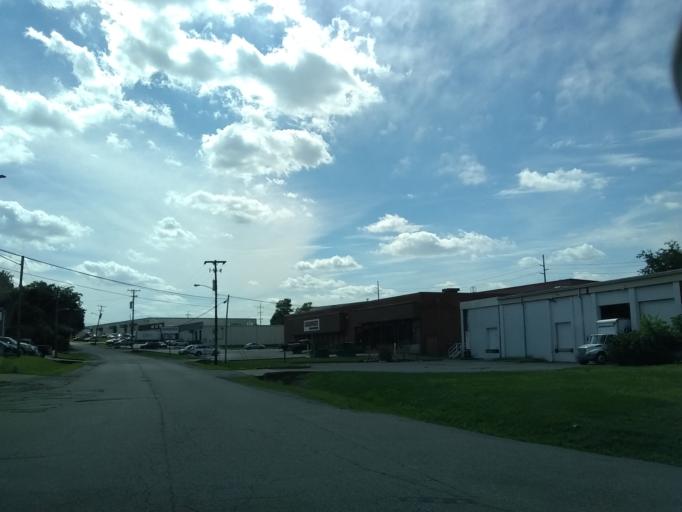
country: US
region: Tennessee
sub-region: Davidson County
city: Nashville
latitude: 36.1515
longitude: -86.7005
